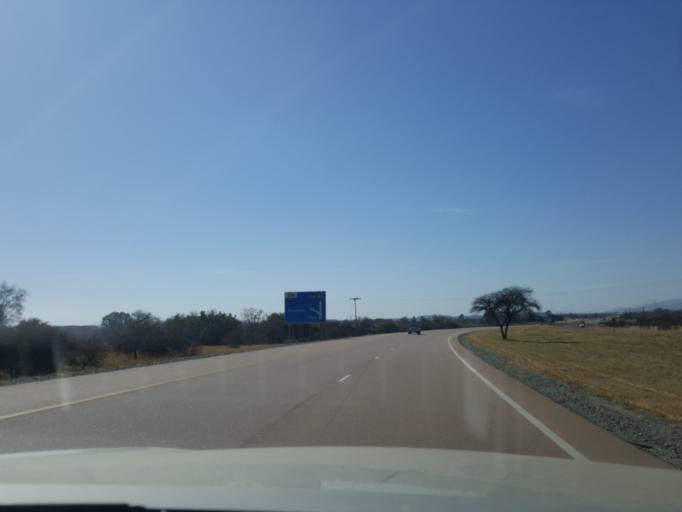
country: ZA
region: North-West
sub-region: Bojanala Platinum District Municipality
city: Brits
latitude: -25.7383
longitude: 27.5401
